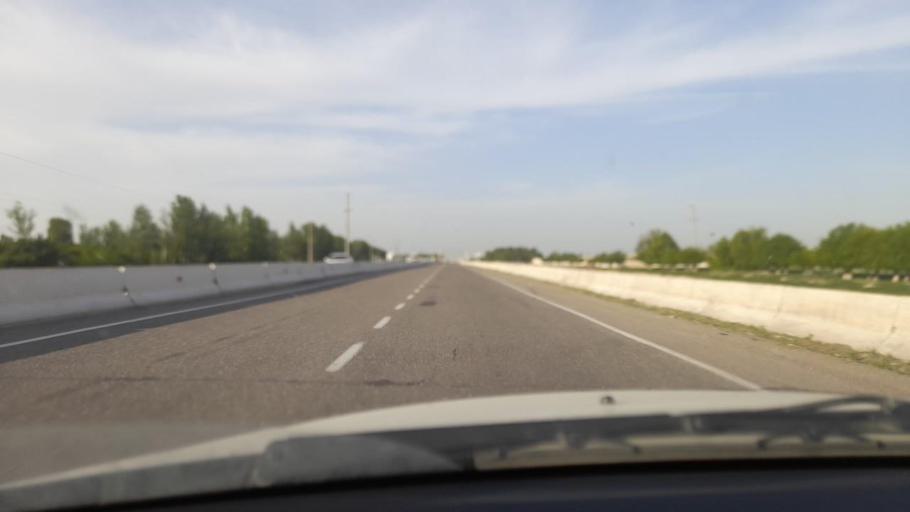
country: UZ
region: Jizzax
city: Paxtakor
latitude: 40.3092
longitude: 68.0823
